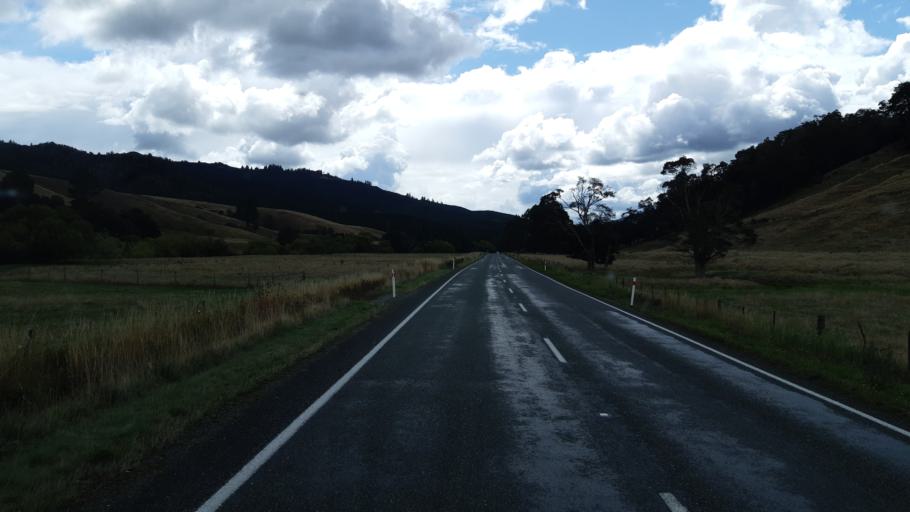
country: NZ
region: Tasman
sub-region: Tasman District
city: Wakefield
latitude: -41.5686
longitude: 172.7766
